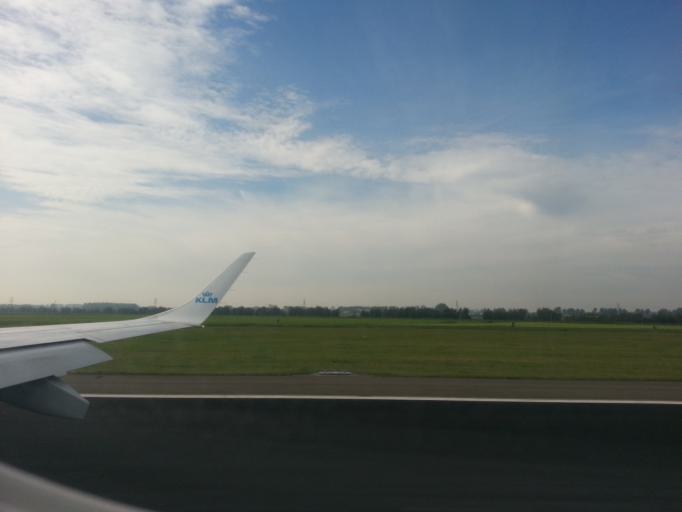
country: NL
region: North Holland
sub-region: Gemeente Haarlemmermeer
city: Hoofddorp
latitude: 52.3556
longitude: 4.7114
